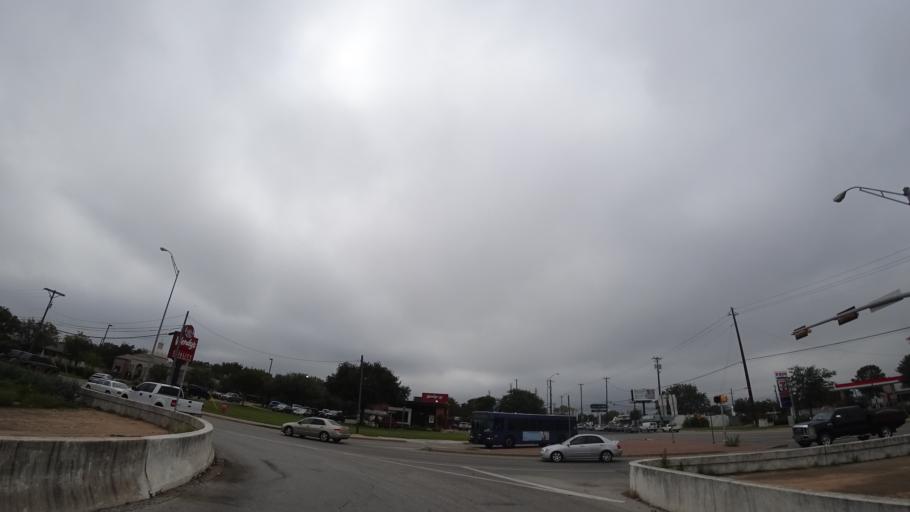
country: US
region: Texas
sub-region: Travis County
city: Austin
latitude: 30.2225
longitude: -97.7638
